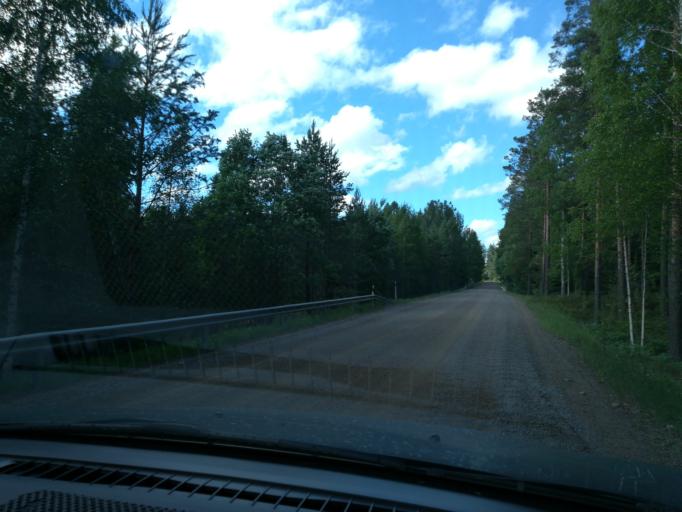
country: FI
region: South Karelia
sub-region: Lappeenranta
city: Savitaipale
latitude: 61.2904
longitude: 27.6575
